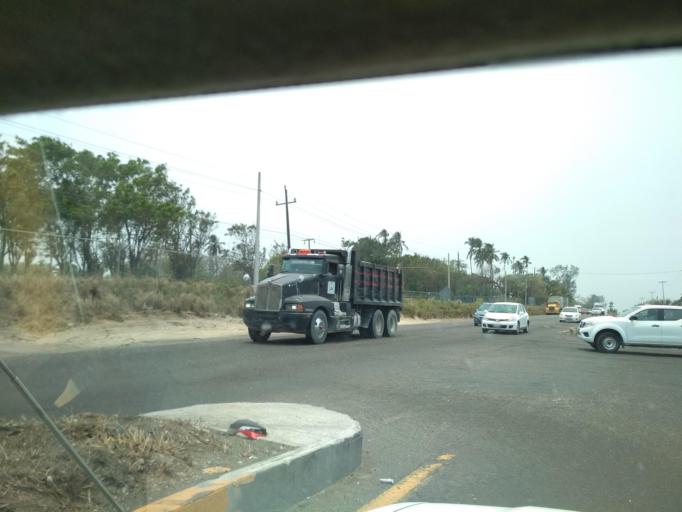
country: MX
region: Veracruz
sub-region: Veracruz
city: Delfino Victoria (Santa Fe)
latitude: 19.1797
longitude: -96.2505
